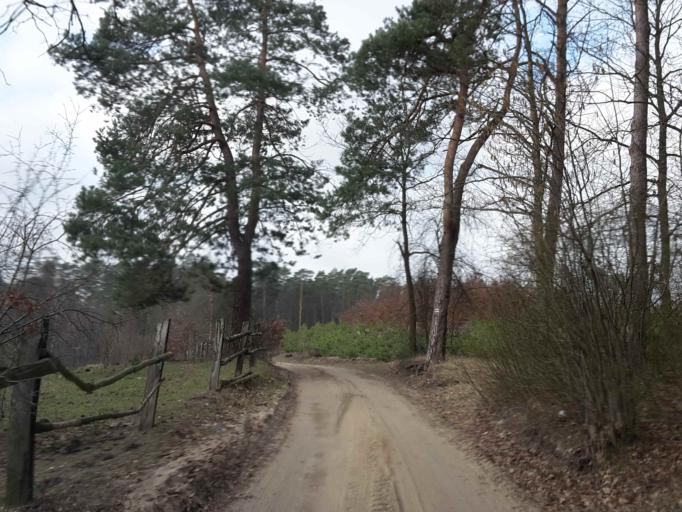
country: PL
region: Kujawsko-Pomorskie
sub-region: Powiat brodnicki
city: Brodnica
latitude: 53.3240
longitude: 19.3576
